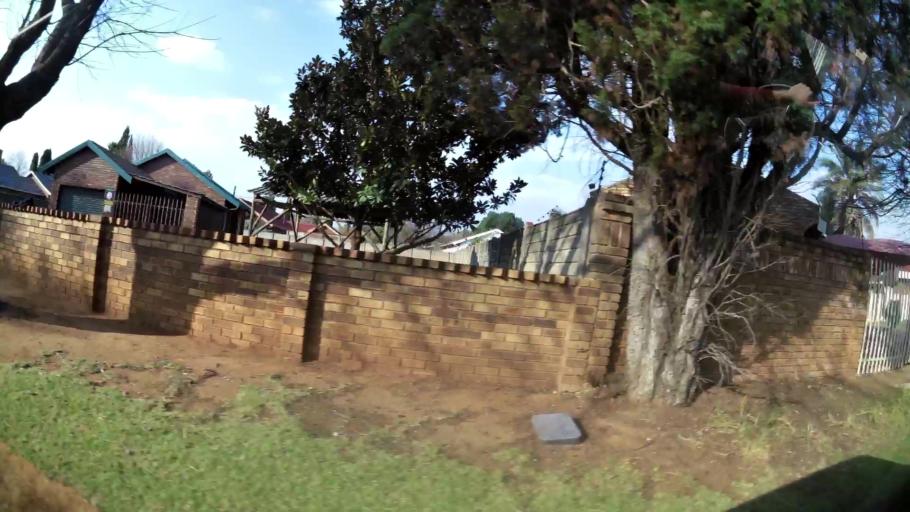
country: ZA
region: Gauteng
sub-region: Ekurhuleni Metropolitan Municipality
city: Benoni
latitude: -26.1269
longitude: 28.3692
